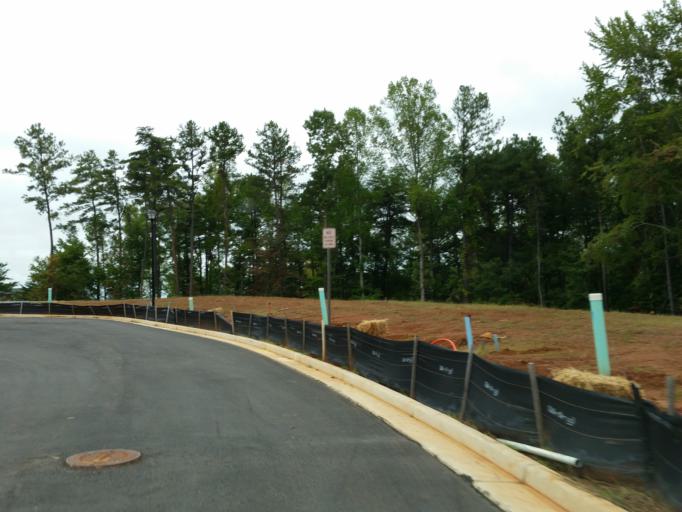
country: US
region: Georgia
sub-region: Cherokee County
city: Woodstock
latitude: 34.0830
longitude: -84.4645
